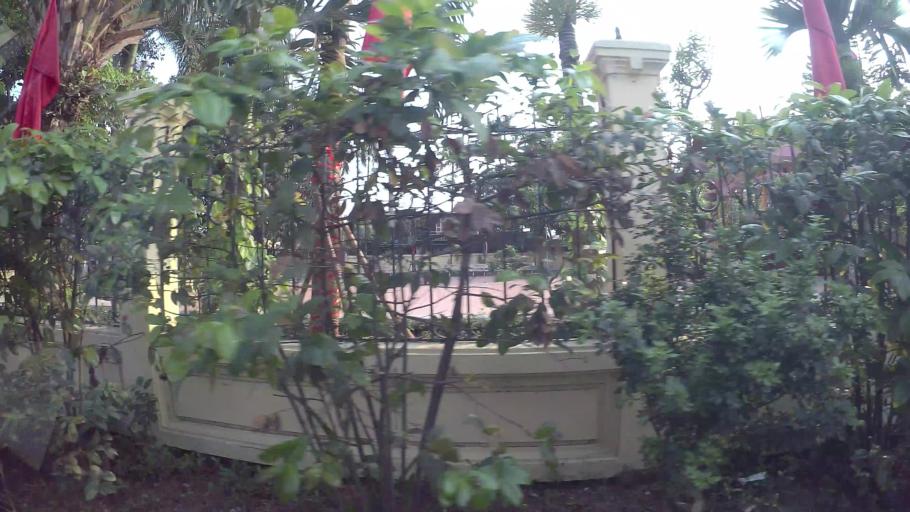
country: VN
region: Ha Noi
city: Thanh Xuan
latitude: 20.9818
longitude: 105.8300
